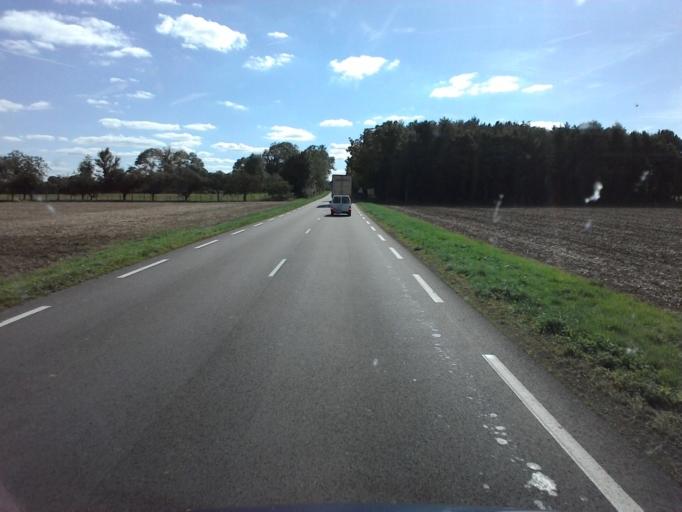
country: FR
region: Bourgogne
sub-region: Departement de la Cote-d'Or
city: Chatillon-sur-Seine
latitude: 47.7548
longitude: 4.4979
